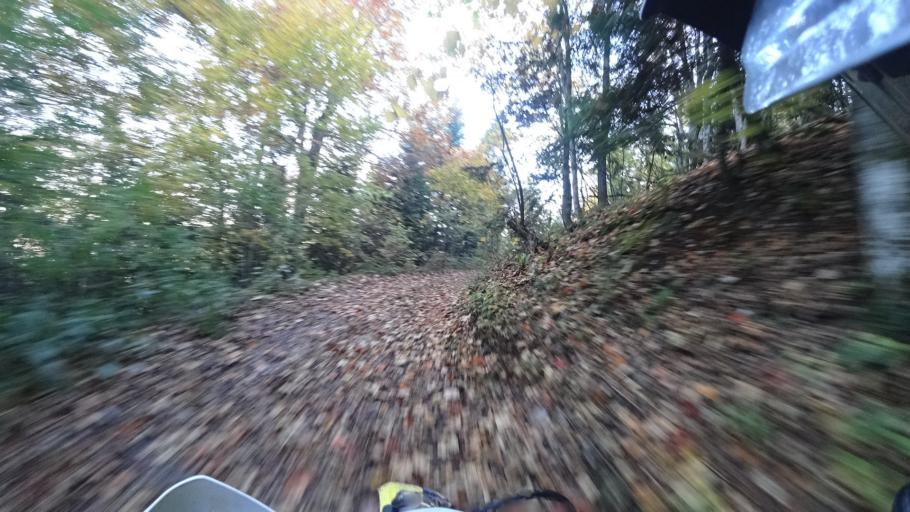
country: HR
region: Karlovacka
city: Plaski
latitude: 44.9726
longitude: 15.4314
